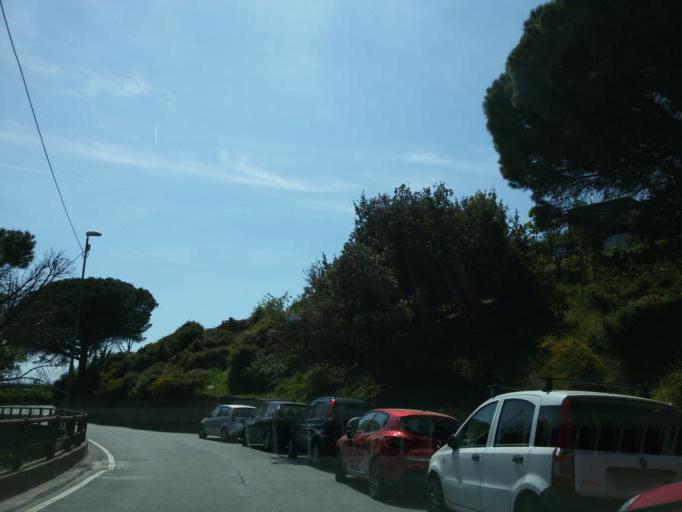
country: IT
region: Liguria
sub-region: Provincia di Genova
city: Genoa
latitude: 44.4239
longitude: 8.9566
